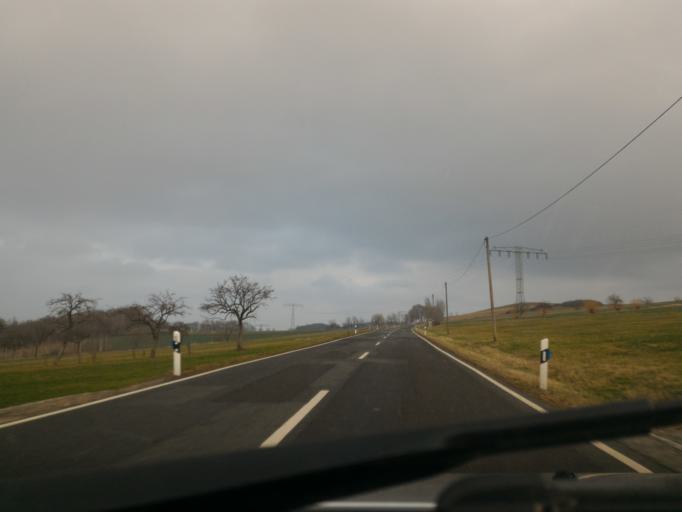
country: DE
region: Saxony
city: Grossschonau
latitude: 50.8961
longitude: 14.6946
